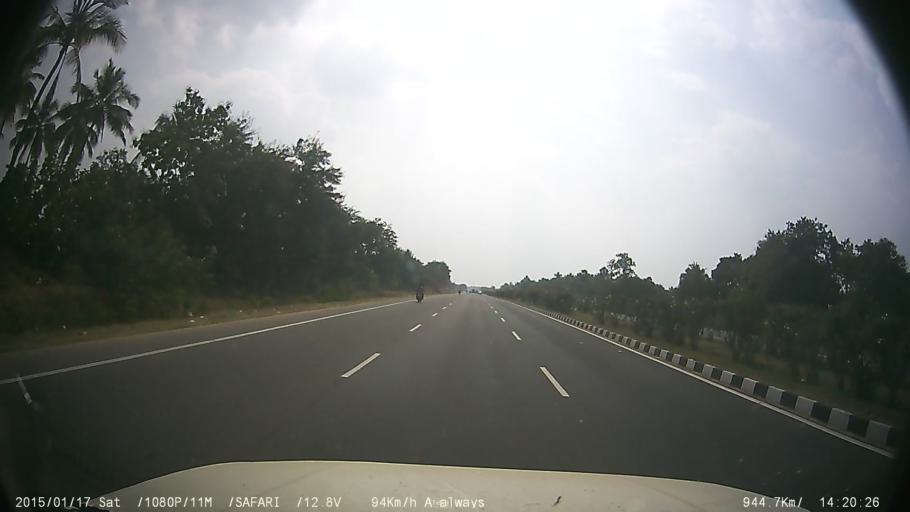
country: IN
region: Tamil Nadu
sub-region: Vellore
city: Vaniyambadi
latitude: 12.7096
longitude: 78.6518
